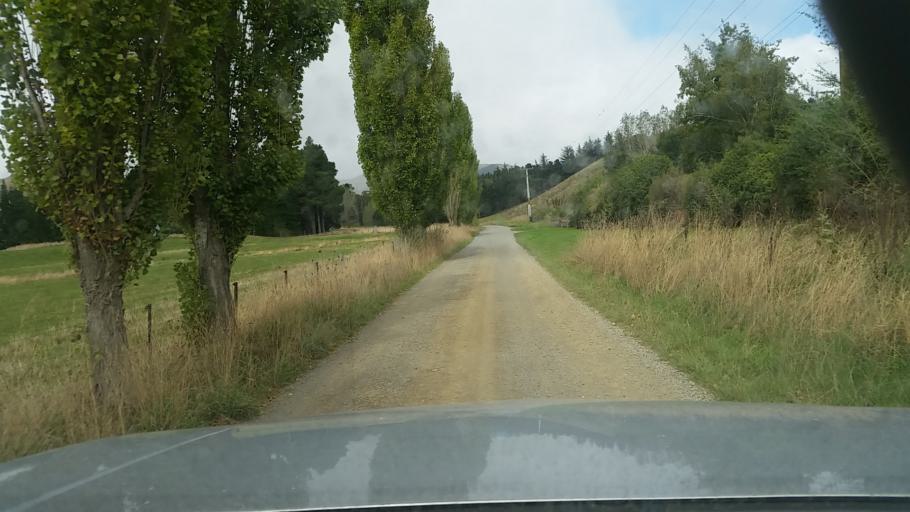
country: NZ
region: Marlborough
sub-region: Marlborough District
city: Blenheim
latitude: -41.7299
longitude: 173.9227
